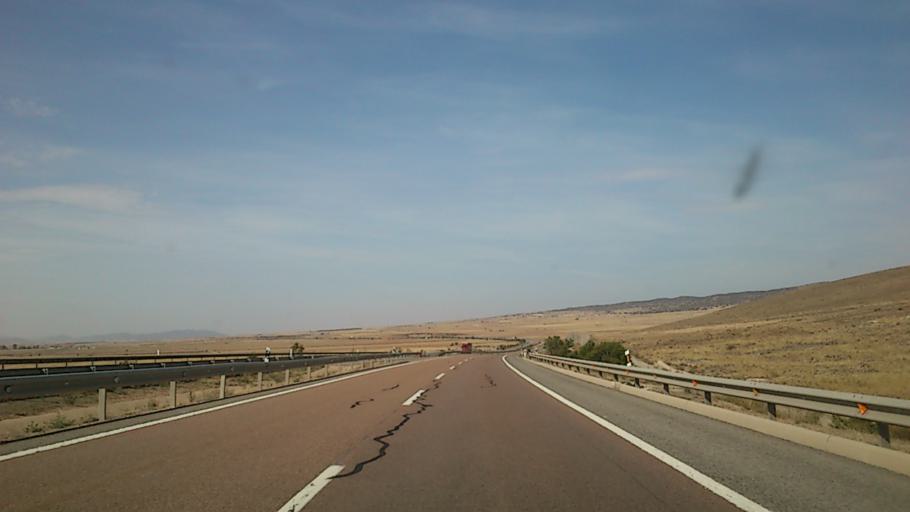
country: ES
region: Aragon
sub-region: Provincia de Teruel
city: Singra
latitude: 40.6589
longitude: -1.3179
